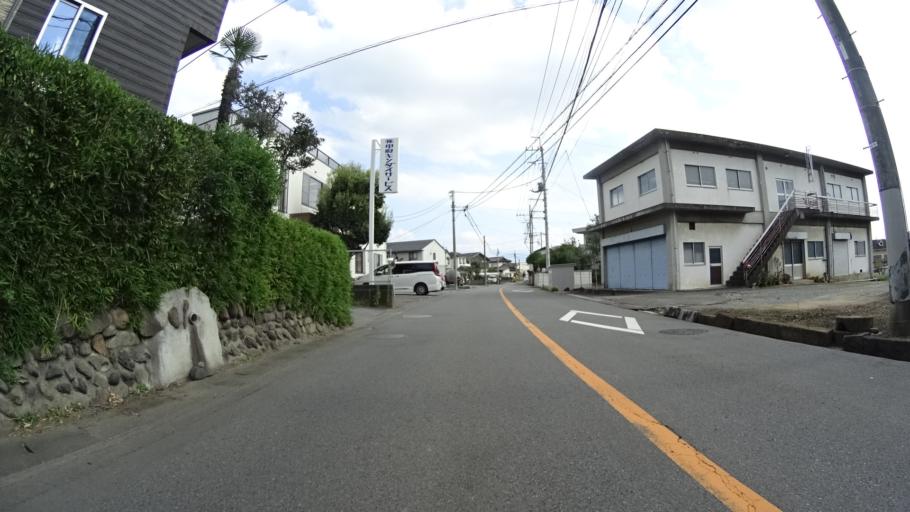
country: JP
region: Yamanashi
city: Kofu-shi
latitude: 35.6850
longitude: 138.5660
